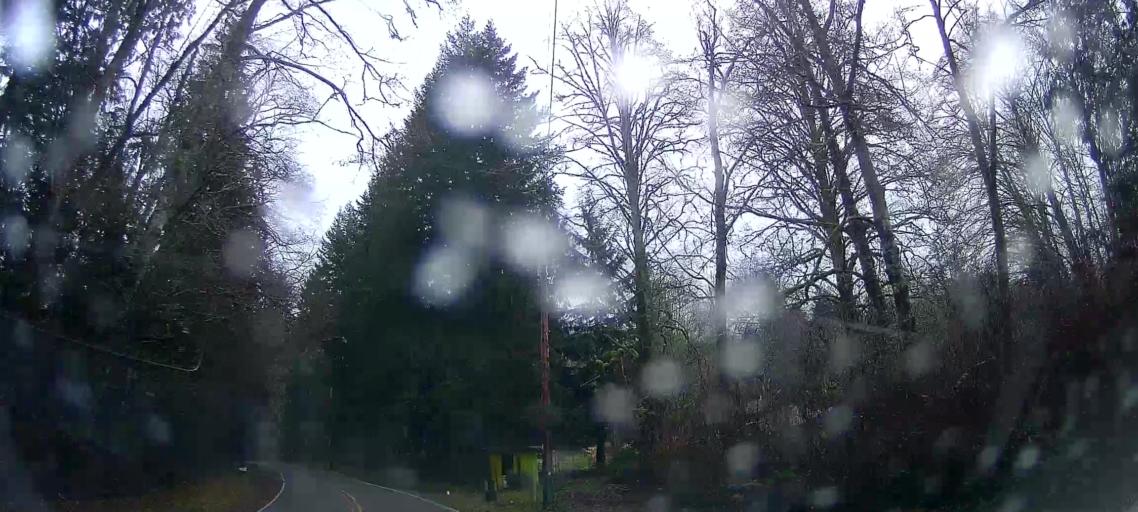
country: US
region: Washington
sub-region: Skagit County
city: Clear Lake
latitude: 48.4682
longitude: -122.1760
